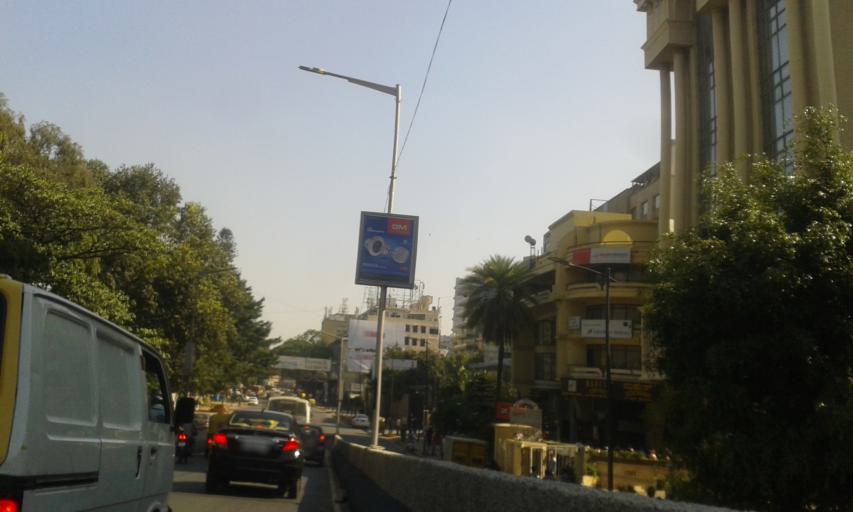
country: IN
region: Karnataka
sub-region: Bangalore Urban
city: Bangalore
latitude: 12.9656
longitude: 77.5975
